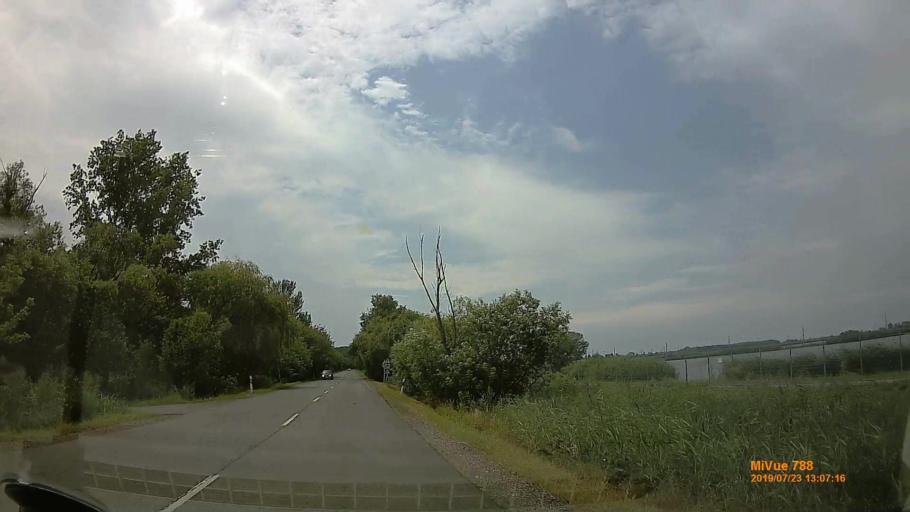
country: HU
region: Szabolcs-Szatmar-Bereg
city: Tiszavasvari
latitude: 47.9581
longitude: 21.3391
